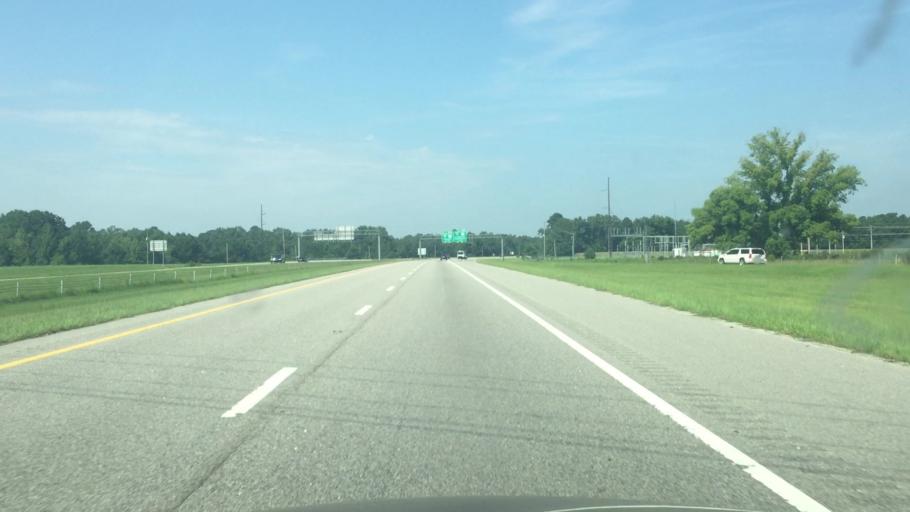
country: US
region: North Carolina
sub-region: Robeson County
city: Lumberton
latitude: 34.5924
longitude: -79.0917
